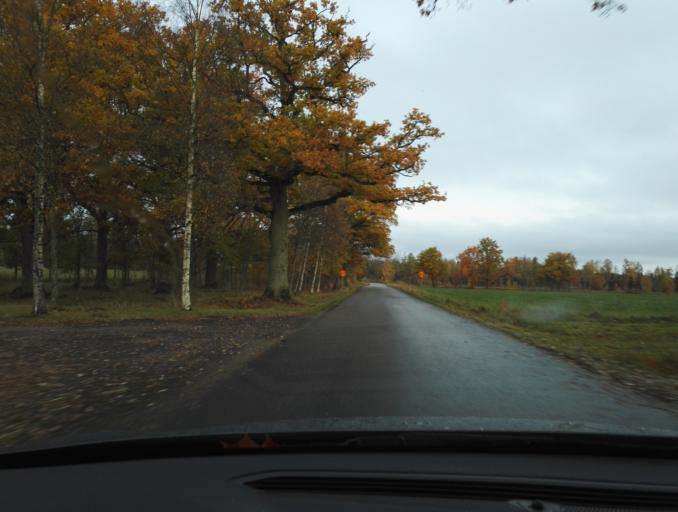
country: SE
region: Kronoberg
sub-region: Vaxjo Kommun
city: Vaexjoe
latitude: 56.9142
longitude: 14.7351
